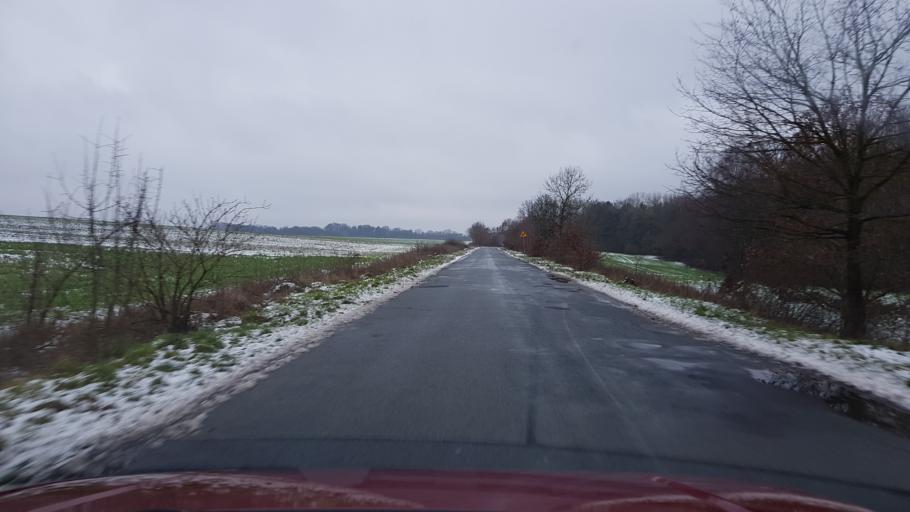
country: PL
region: West Pomeranian Voivodeship
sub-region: Powiat goleniowski
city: Nowogard
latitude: 53.6702
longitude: 15.1975
